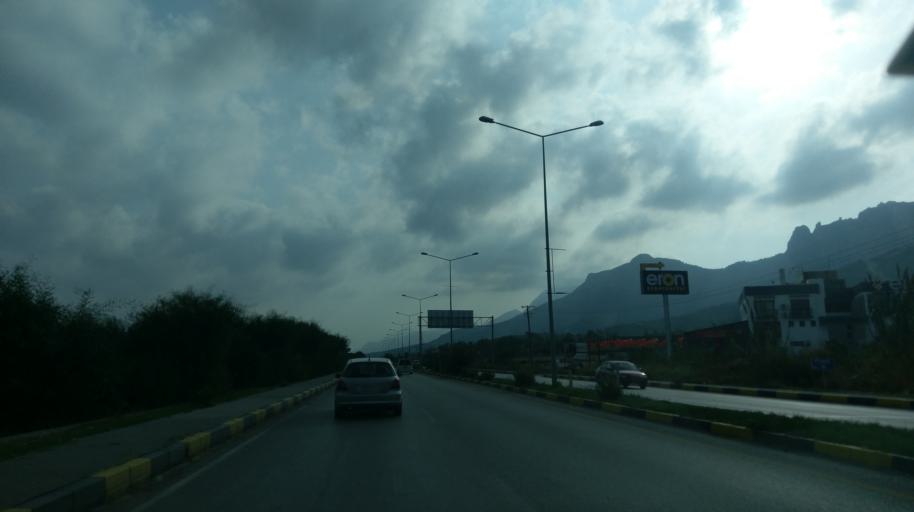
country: CY
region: Keryneia
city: Kyrenia
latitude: 35.3309
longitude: 33.2759
